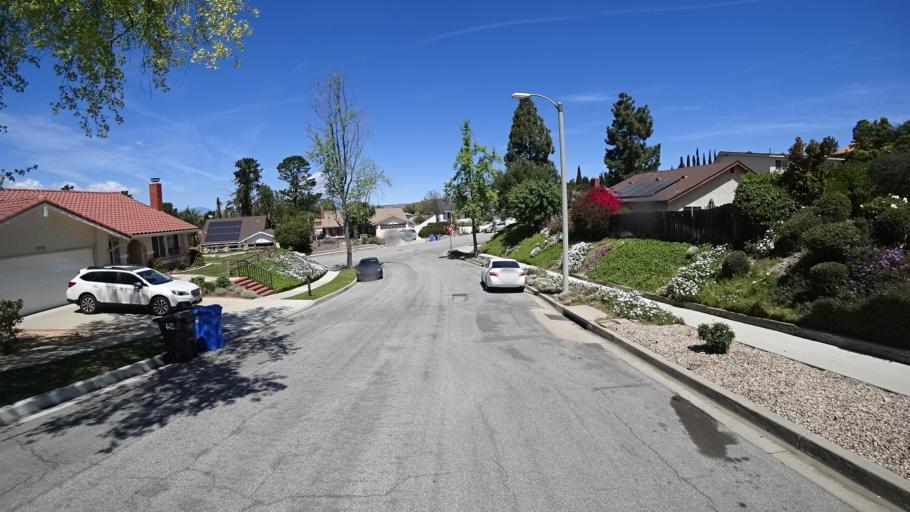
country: US
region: California
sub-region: Ventura County
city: Thousand Oaks
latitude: 34.2304
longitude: -118.8525
